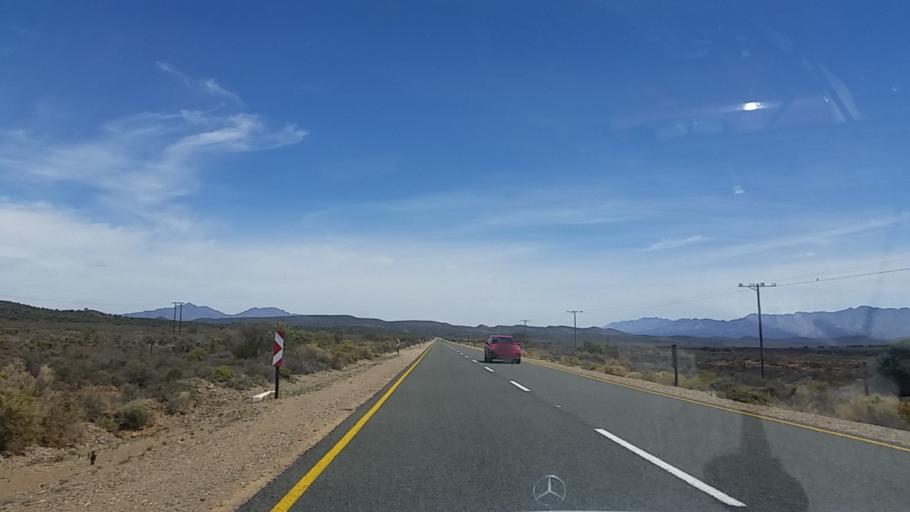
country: ZA
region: Eastern Cape
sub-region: Cacadu District Municipality
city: Willowmore
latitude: -33.5022
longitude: 23.2480
